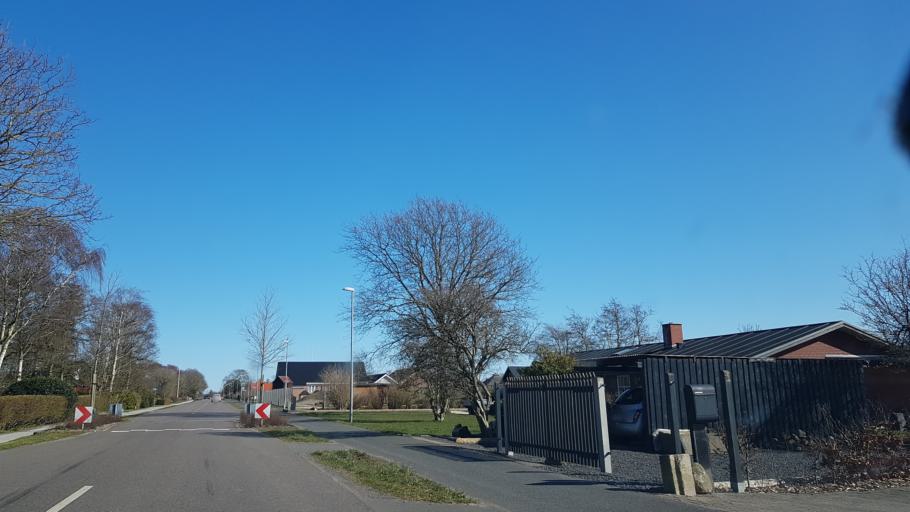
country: DK
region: South Denmark
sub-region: Esbjerg Kommune
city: Ribe
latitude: 55.3153
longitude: 8.7379
